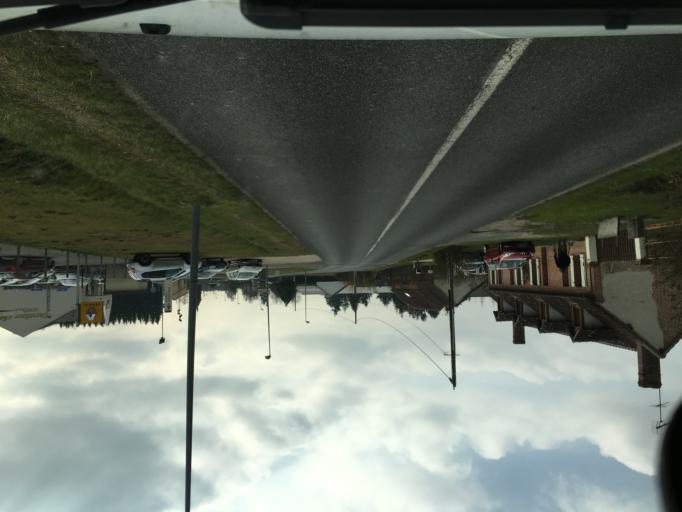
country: FR
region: Centre
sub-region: Departement du Loir-et-Cher
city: Neung-sur-Beuvron
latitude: 47.5257
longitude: 1.8124
